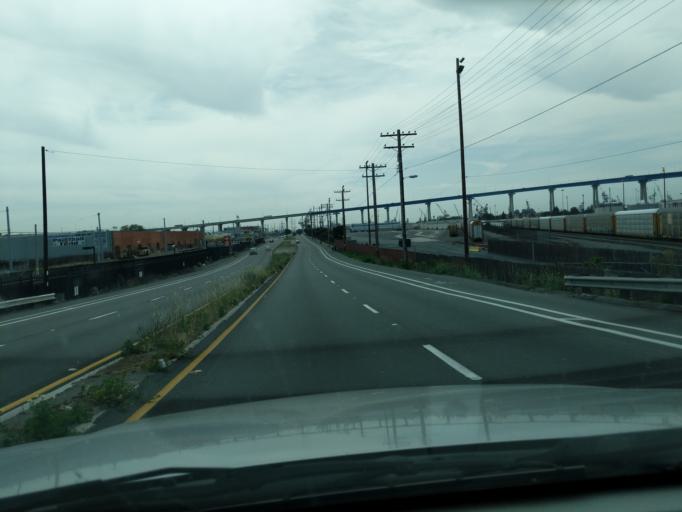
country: US
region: California
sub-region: San Diego County
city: San Diego
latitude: 32.7024
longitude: -117.1537
